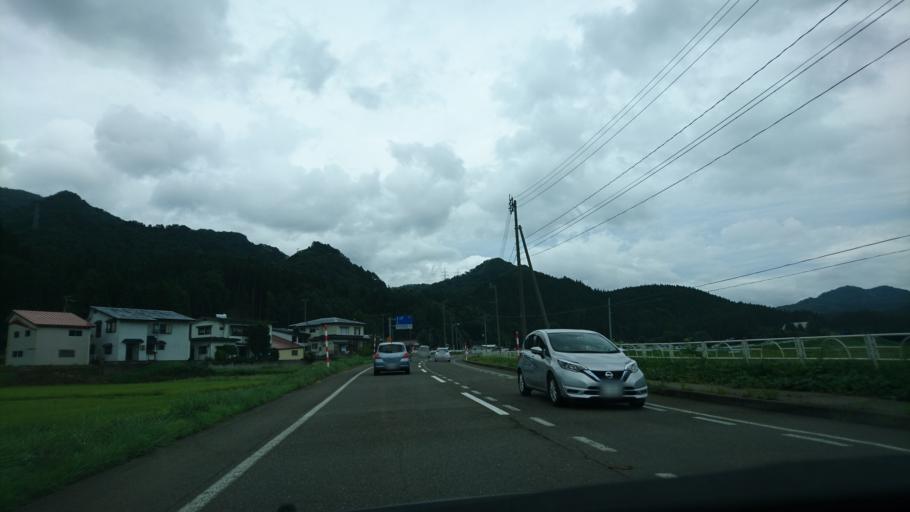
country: JP
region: Akita
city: Yuzawa
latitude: 38.9873
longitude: 140.4805
